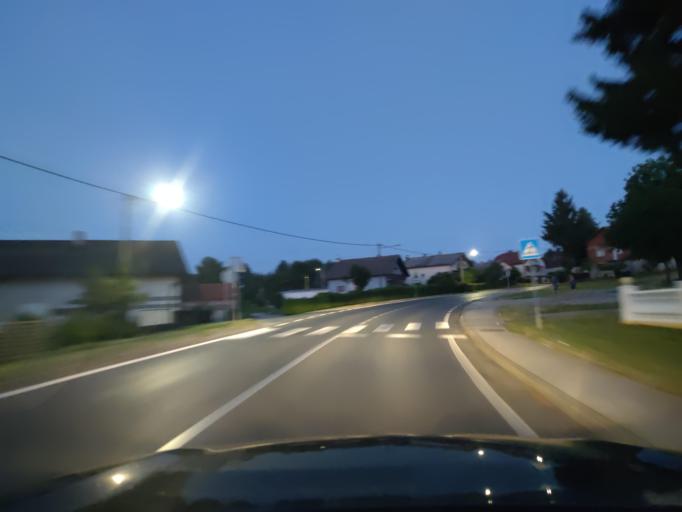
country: HR
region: Medimurska
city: Vratisinec
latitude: 46.4718
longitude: 16.4248
